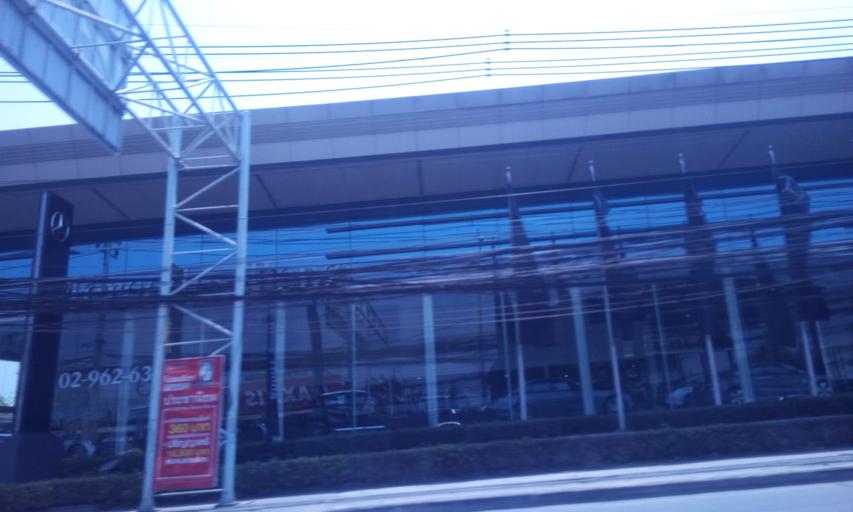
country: TH
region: Nonthaburi
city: Pak Kret
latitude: 13.9066
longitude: 100.5130
